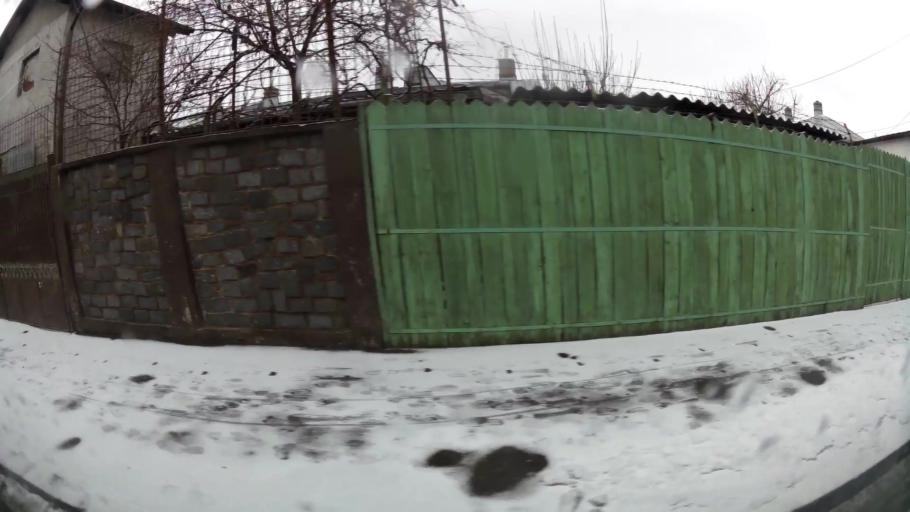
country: RO
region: Prahova
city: Ploiesti
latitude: 44.9489
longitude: 26.0270
